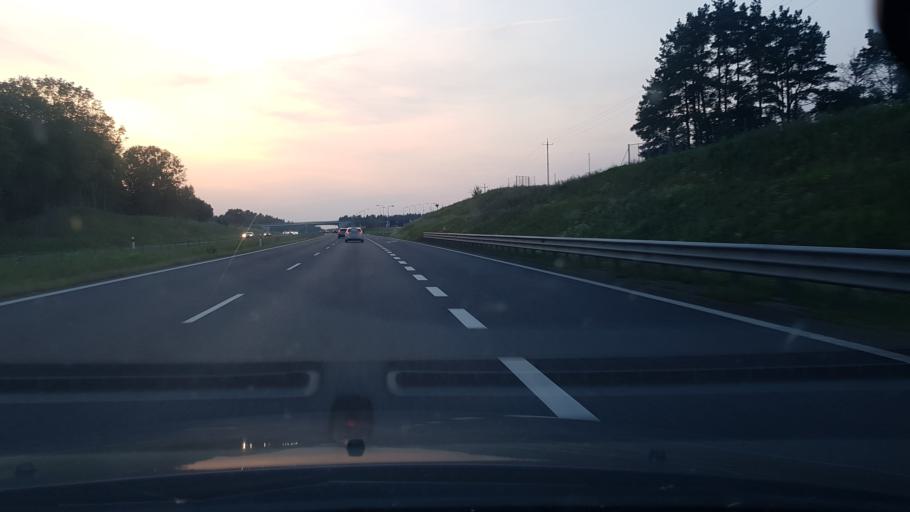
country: PL
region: Warmian-Masurian Voivodeship
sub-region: Powiat olsztynski
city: Olsztynek
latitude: 53.5123
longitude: 20.3015
